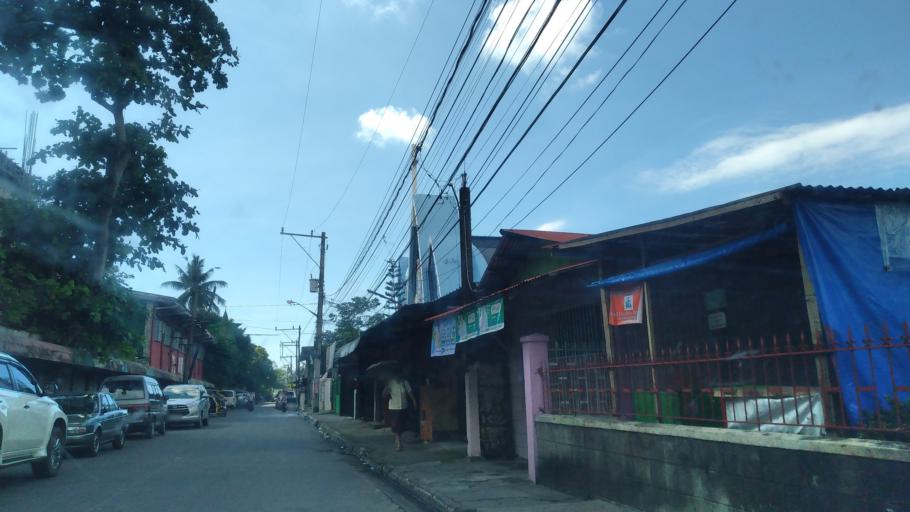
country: PH
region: Calabarzon
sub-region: Province of Quezon
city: Lucena
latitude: 13.9338
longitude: 121.6046
